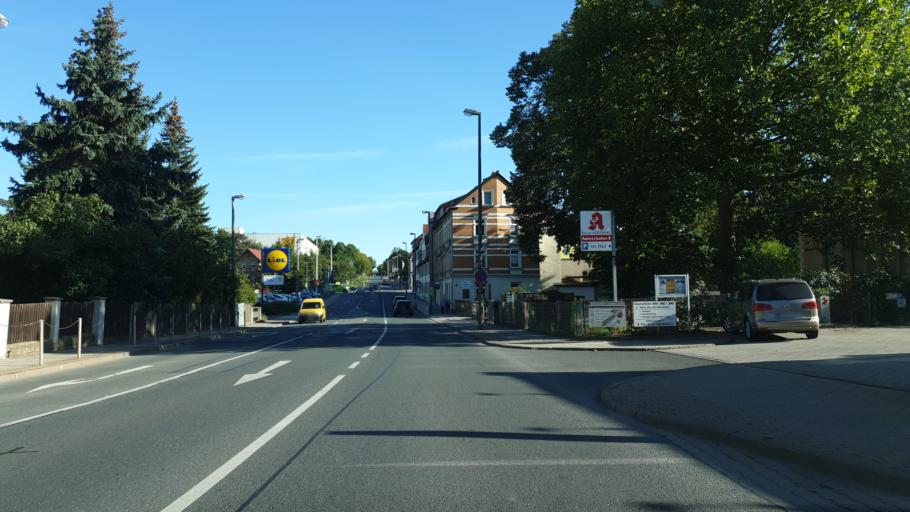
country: DE
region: Thuringia
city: Bad Kostritz
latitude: 50.9191
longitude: 12.0534
